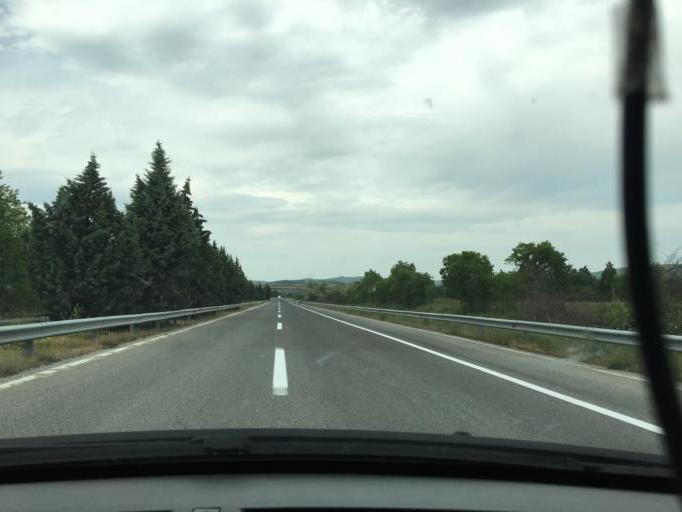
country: MK
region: Negotino
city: Negotino
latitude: 41.5439
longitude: 22.0398
